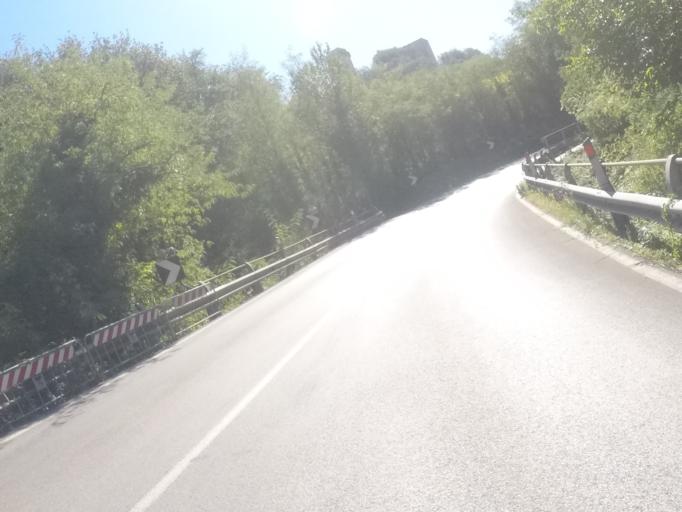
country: IT
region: Tuscany
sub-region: Province of Florence
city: Incisa in Val d'Arno
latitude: 43.6780
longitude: 11.4637
